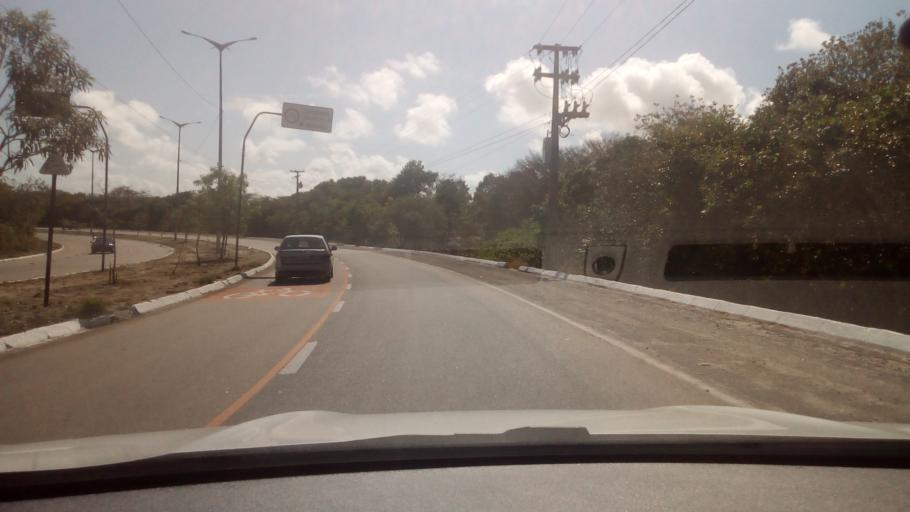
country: BR
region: Paraiba
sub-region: Joao Pessoa
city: Joao Pessoa
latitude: -7.1568
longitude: -34.7993
